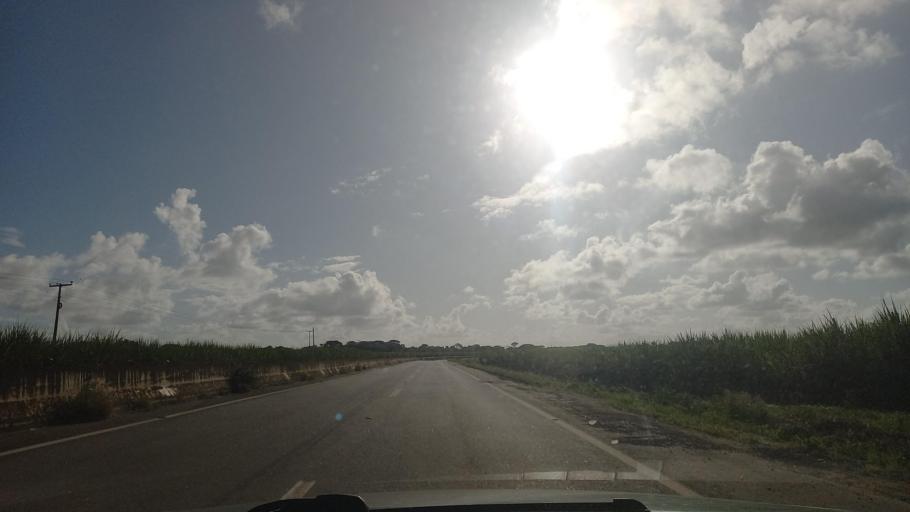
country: BR
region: Alagoas
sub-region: Sao Miguel Dos Campos
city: Sao Miguel dos Campos
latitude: -9.8056
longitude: -36.0001
